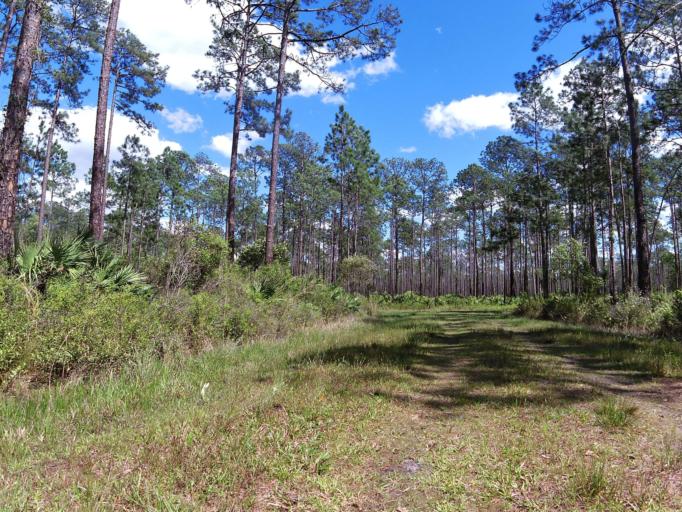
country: US
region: Florida
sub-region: Clay County
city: Green Cove Springs
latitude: 29.9627
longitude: -81.6320
